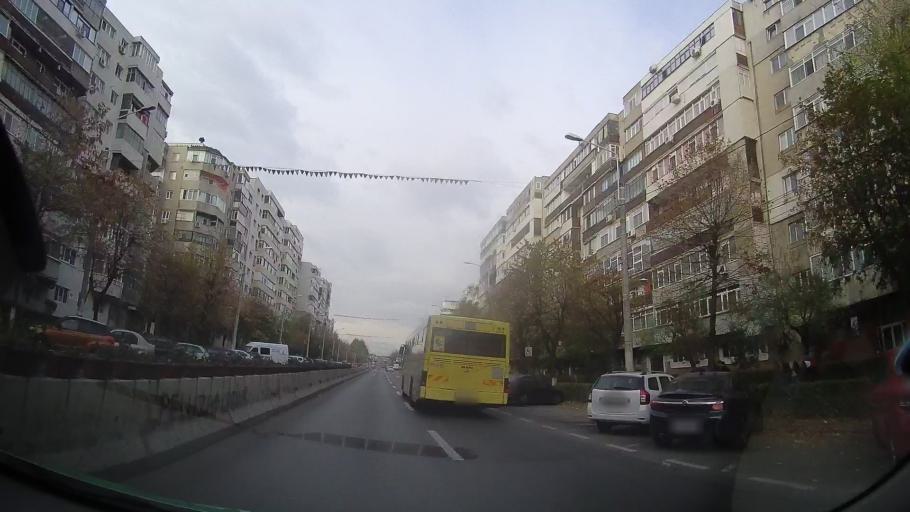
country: RO
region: Prahova
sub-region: Comuna Barcanesti
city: Tatarani
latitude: 44.9199
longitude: 26.0346
